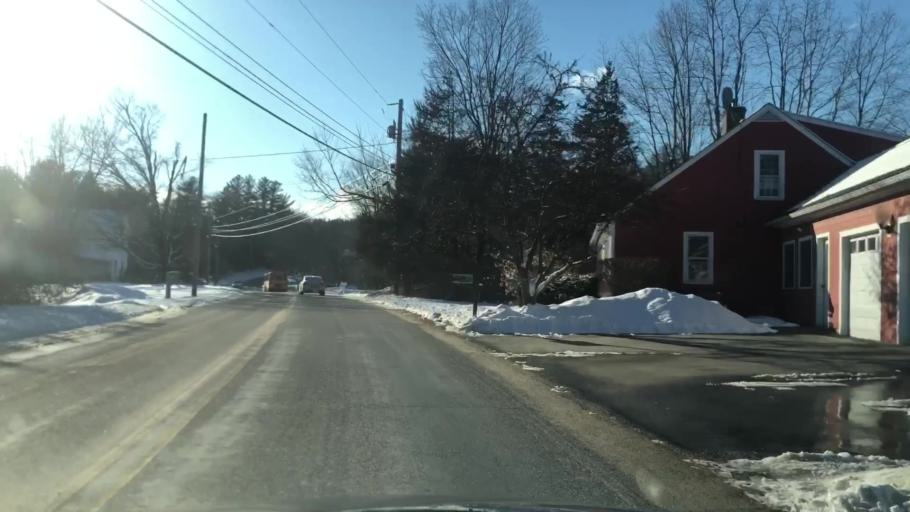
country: US
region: New Hampshire
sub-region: Hillsborough County
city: Milford
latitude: 42.8182
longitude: -71.6865
